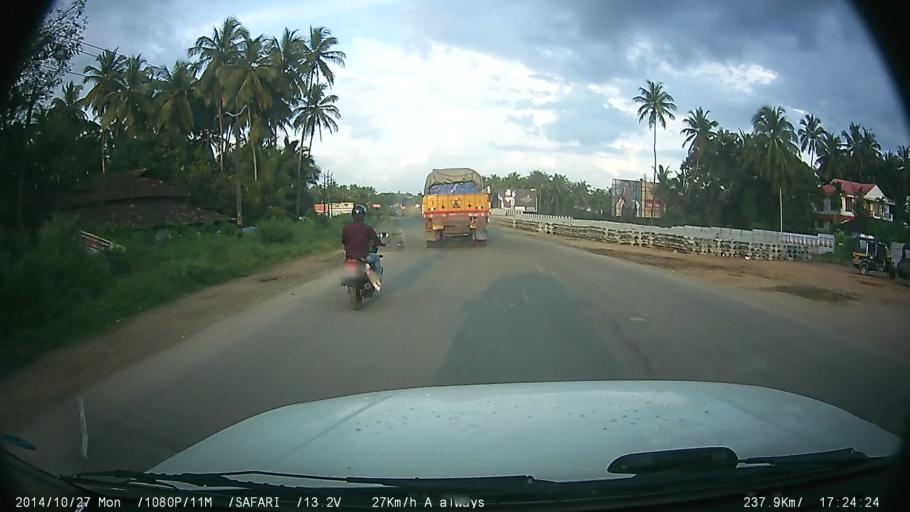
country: IN
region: Kerala
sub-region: Palakkad district
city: Palakkad
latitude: 10.6481
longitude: 76.5608
